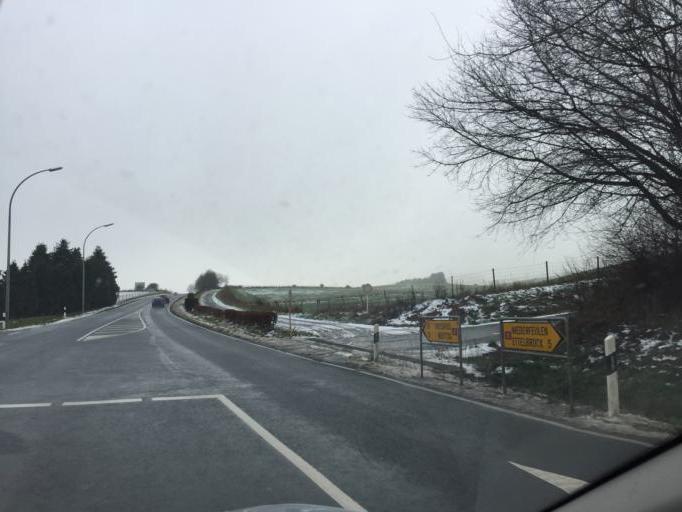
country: LU
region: Diekirch
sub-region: Canton de Diekirch
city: Niederfeulen
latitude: 49.8513
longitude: 6.0373
